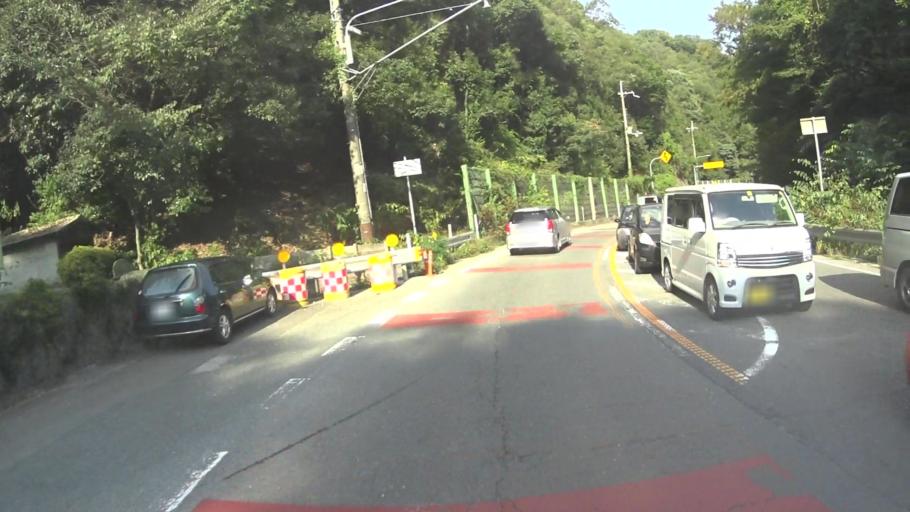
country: JP
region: Kyoto
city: Kameoka
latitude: 34.9916
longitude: 135.6384
